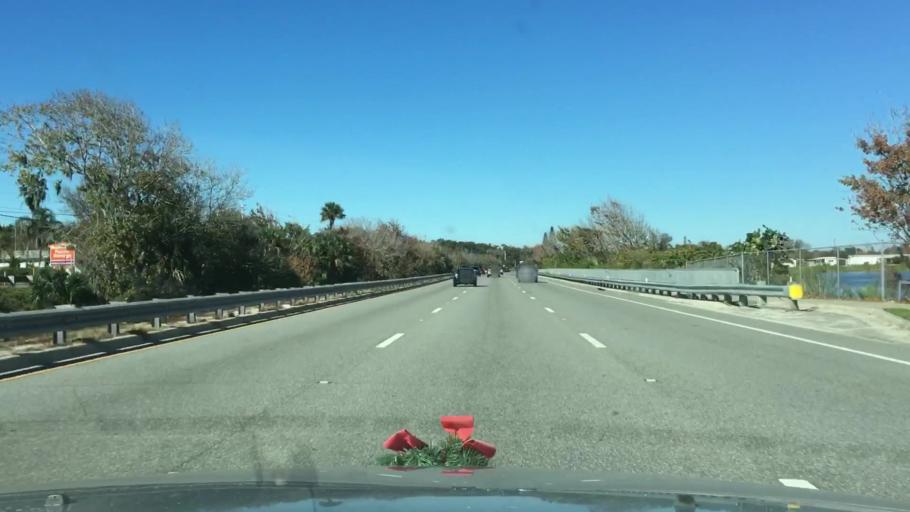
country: US
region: Florida
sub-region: Volusia County
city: South Daytona
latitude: 29.1565
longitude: -81.0207
